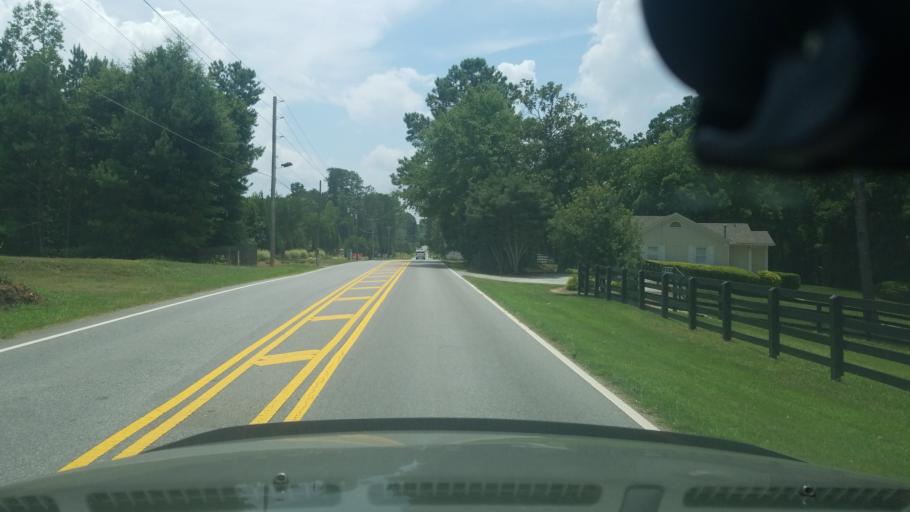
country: US
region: Georgia
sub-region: Fulton County
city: Milton
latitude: 34.1810
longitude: -84.2718
